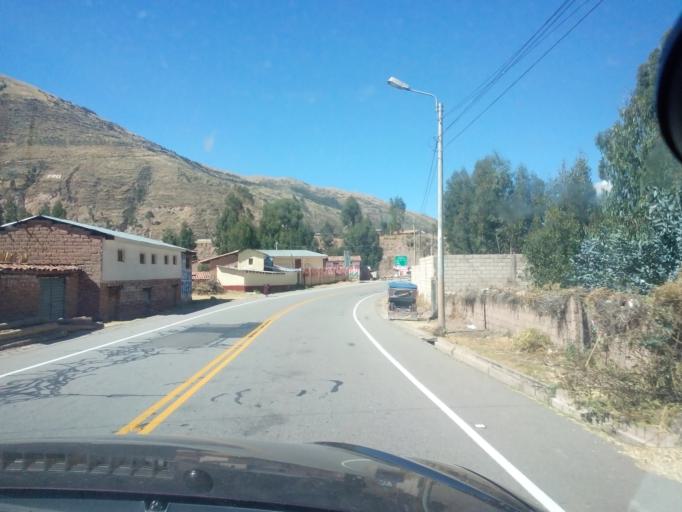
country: PE
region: Cusco
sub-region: Provincia de Canchis
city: Checacupe
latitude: -14.0248
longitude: -71.4571
